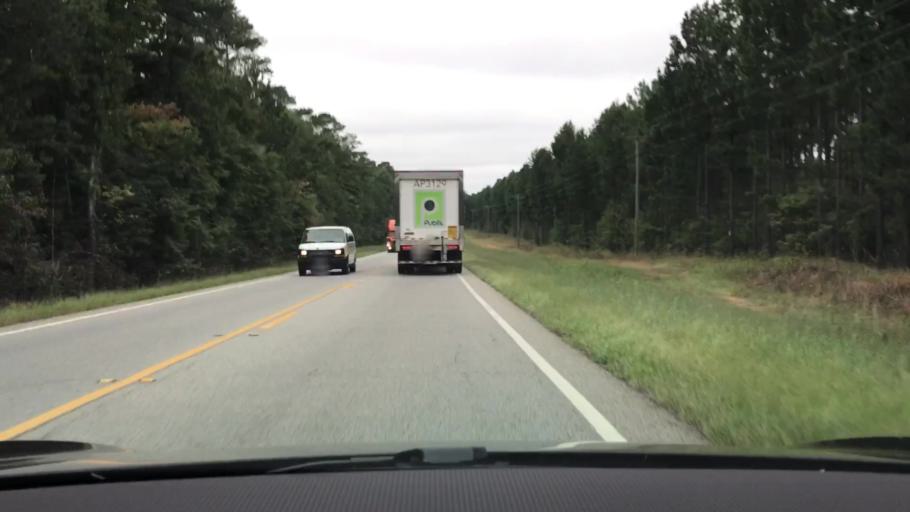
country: US
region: Georgia
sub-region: Greene County
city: Greensboro
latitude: 33.6647
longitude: -83.2478
